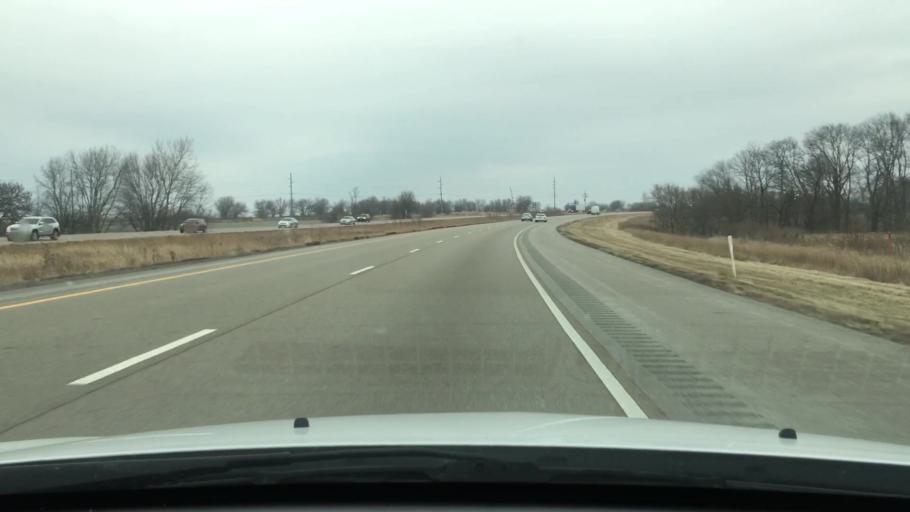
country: US
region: Illinois
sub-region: Logan County
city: Atlanta
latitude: 40.2733
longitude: -89.2126
